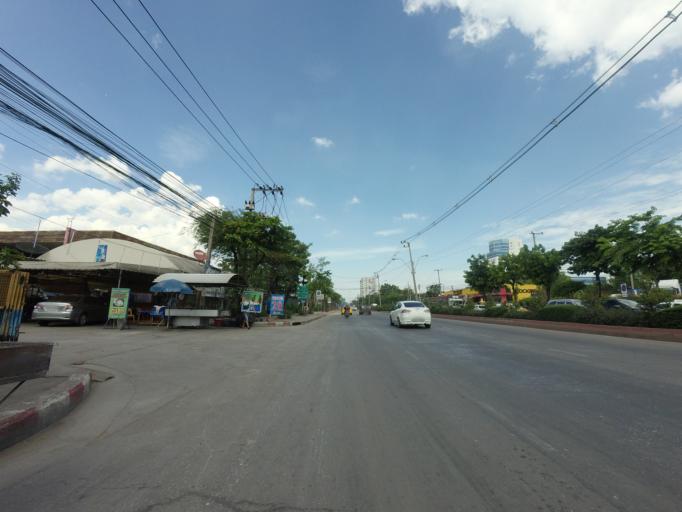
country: TH
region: Bangkok
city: Khlong Toei
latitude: 13.7162
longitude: 100.5618
